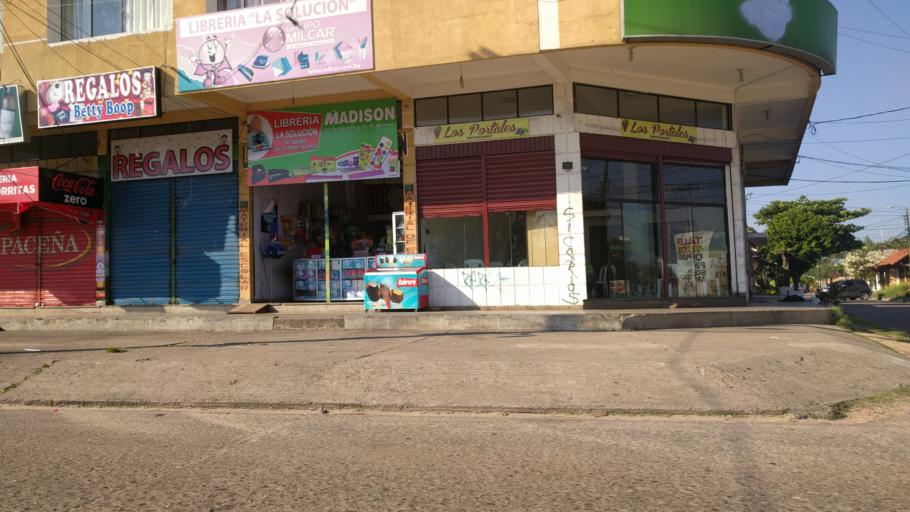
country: BO
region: Santa Cruz
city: Santa Cruz de la Sierra
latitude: -17.8143
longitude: -63.1838
